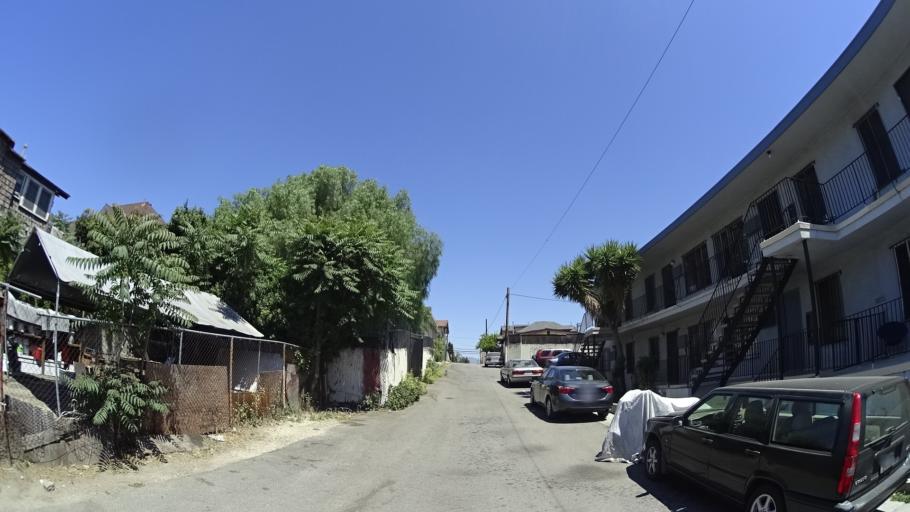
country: US
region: California
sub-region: Los Angeles County
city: Echo Park
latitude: 34.0669
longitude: -118.2628
